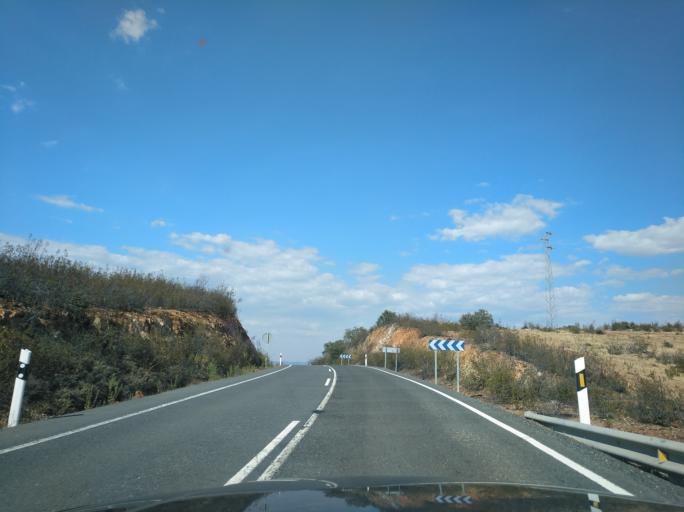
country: ES
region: Andalusia
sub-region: Provincia de Huelva
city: Cabezas Rubias
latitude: 37.6776
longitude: -7.1091
